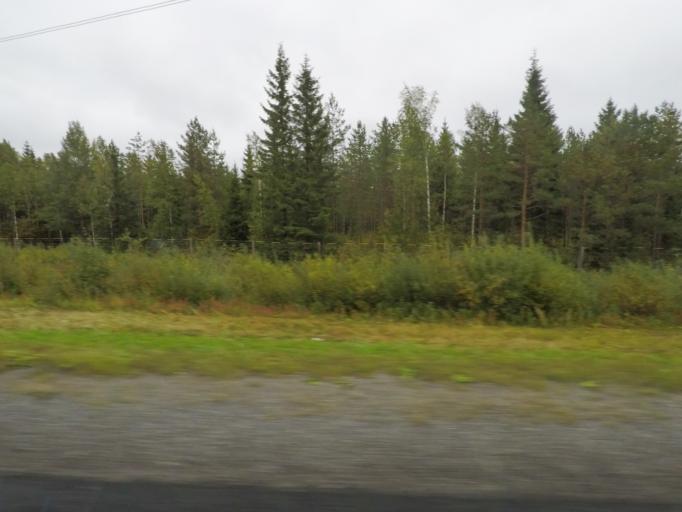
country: FI
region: Northern Savo
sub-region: Kuopio
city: Kuopio
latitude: 62.7525
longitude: 27.5810
